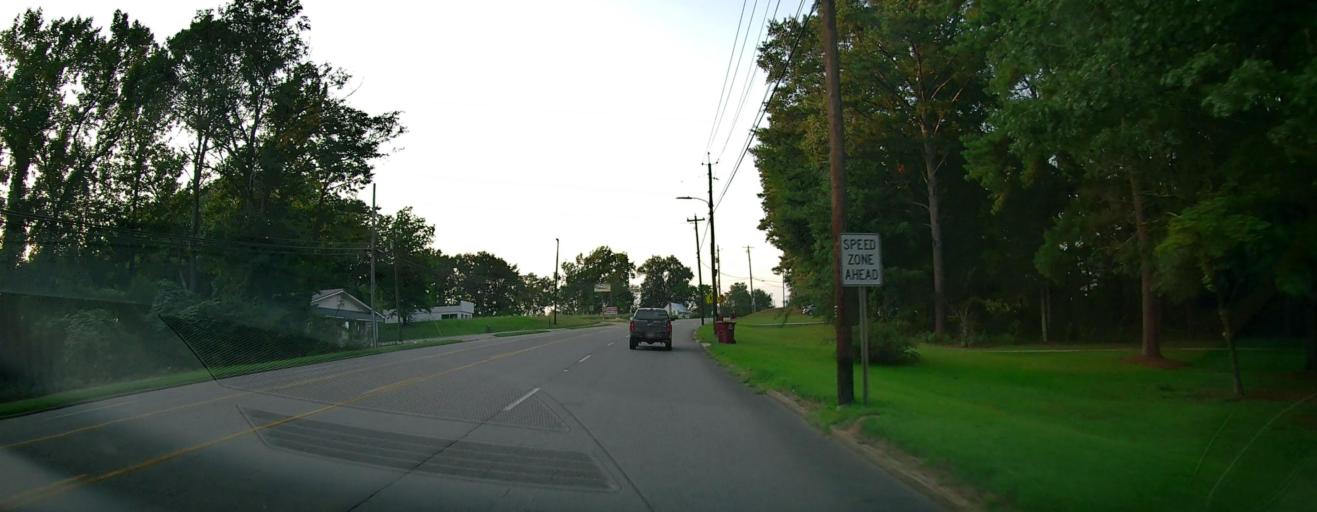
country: US
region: Alabama
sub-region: Marion County
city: Hamilton
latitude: 34.1347
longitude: -87.9903
